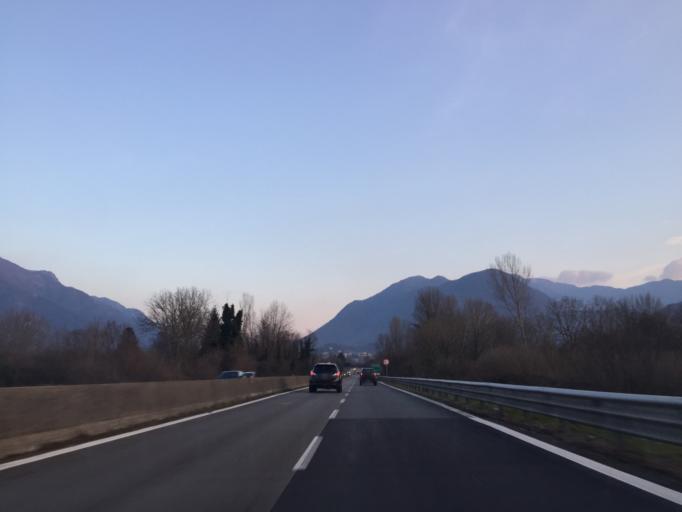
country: IT
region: Campania
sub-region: Provincia di Avellino
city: San Michele di Serino
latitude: 40.8711
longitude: 14.8539
